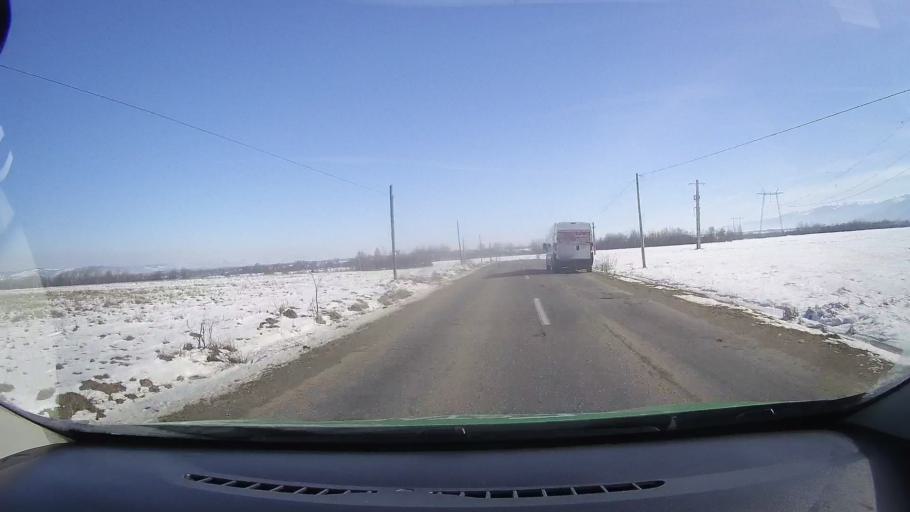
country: RO
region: Brasov
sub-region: Oras Victoria
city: Victoria
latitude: 45.7342
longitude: 24.7291
